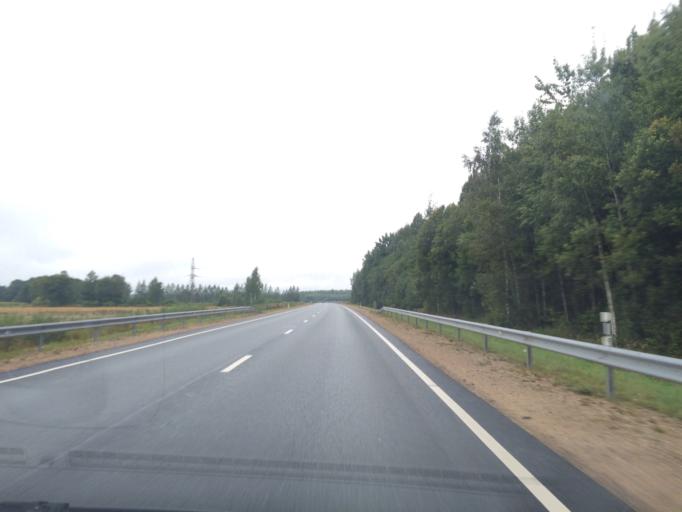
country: LV
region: Lielvarde
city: Lielvarde
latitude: 56.8169
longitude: 24.8365
